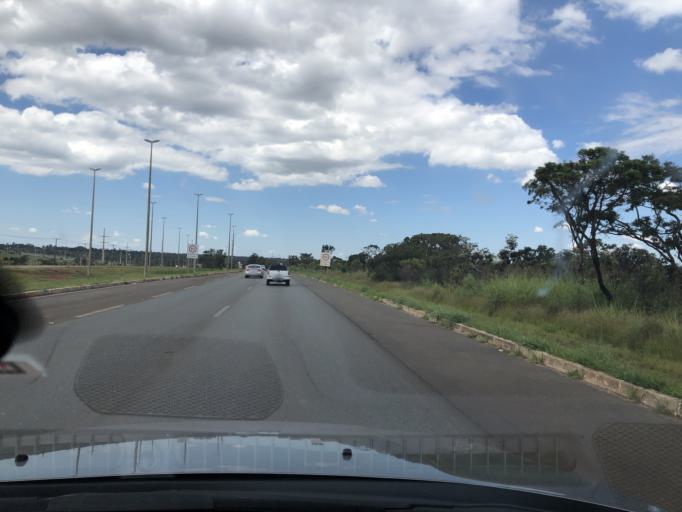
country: BR
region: Federal District
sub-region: Brasilia
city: Brasilia
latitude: -15.9729
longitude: -48.0147
